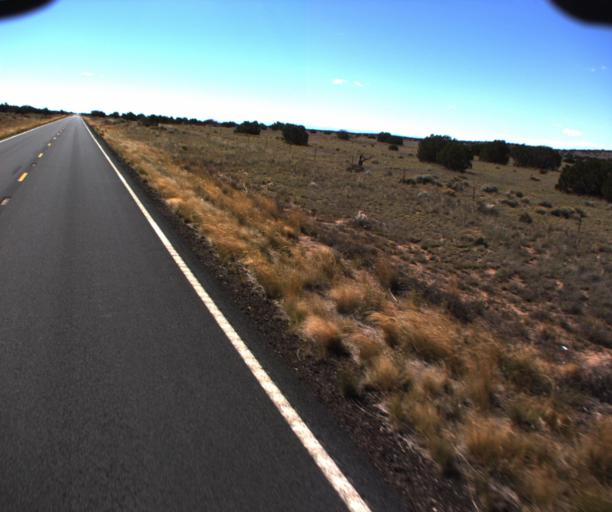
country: US
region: Arizona
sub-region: Apache County
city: Houck
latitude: 34.9163
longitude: -109.2382
